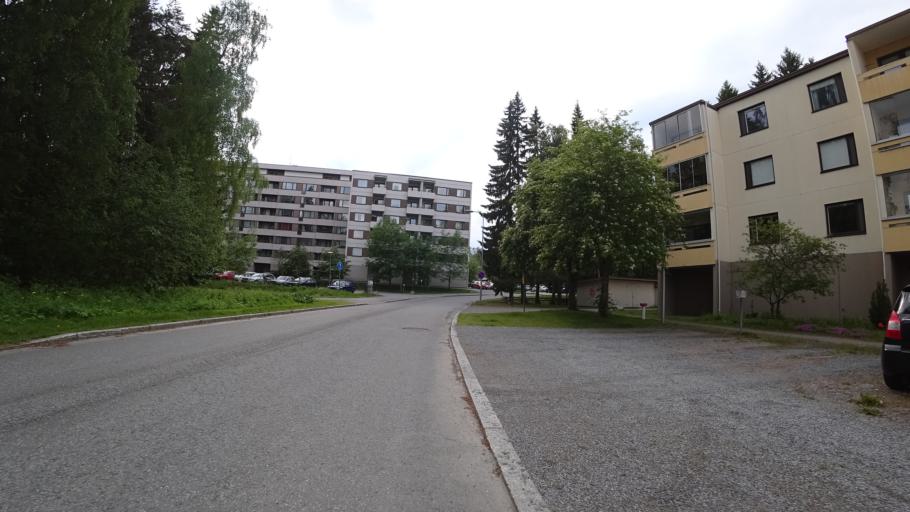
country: FI
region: Pirkanmaa
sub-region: Tampere
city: Pirkkala
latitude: 61.5037
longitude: 23.6192
